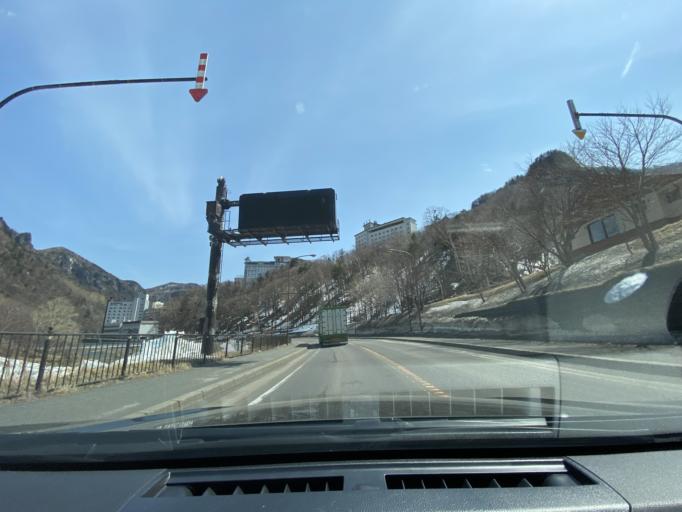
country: JP
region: Hokkaido
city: Kamikawa
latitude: 43.7271
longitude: 142.9481
